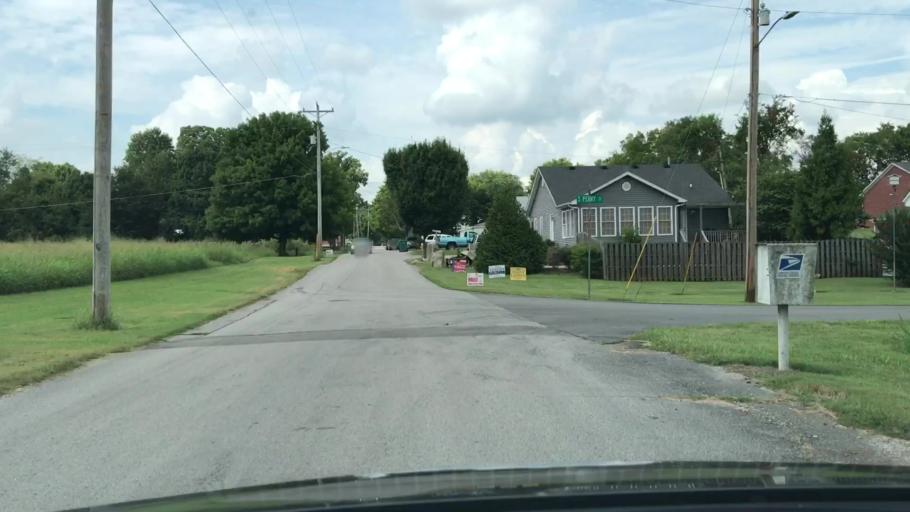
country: US
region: Kentucky
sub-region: Todd County
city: Elkton
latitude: 36.8059
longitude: -87.1508
